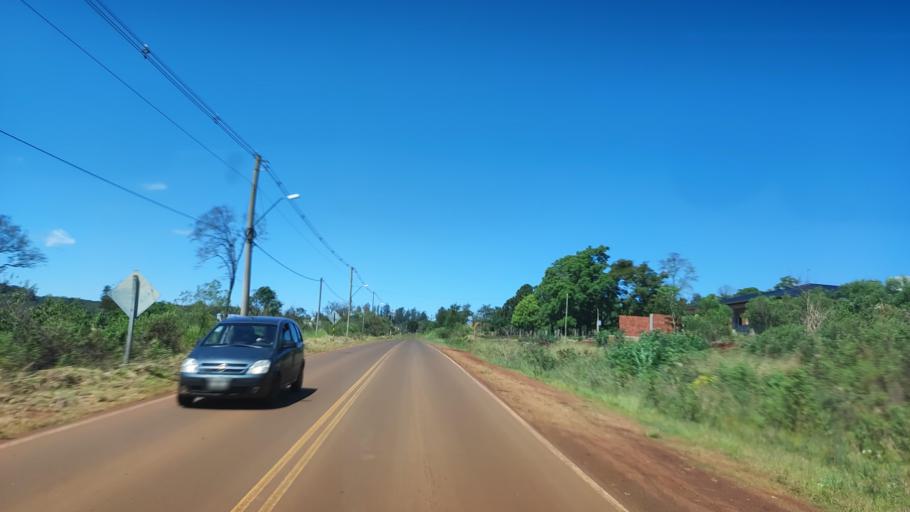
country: AR
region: Misiones
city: Puerto Rico
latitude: -26.8124
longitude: -55.0078
